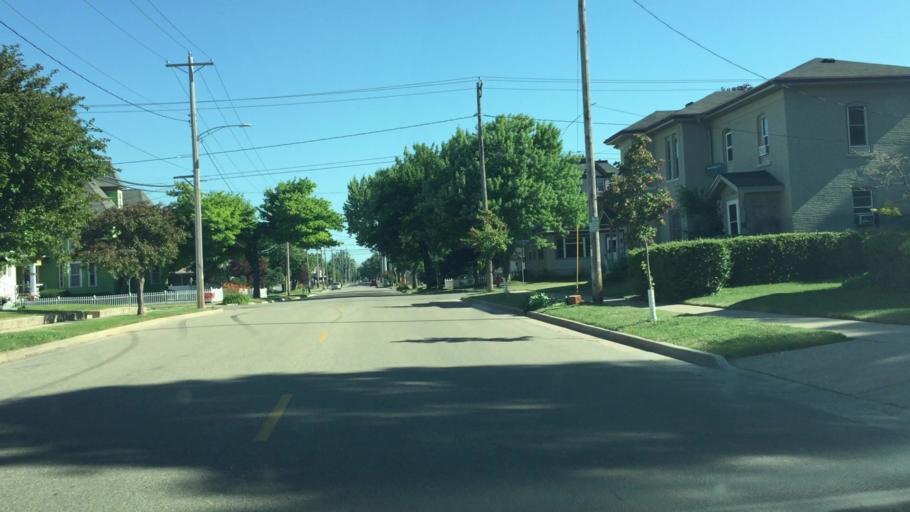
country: US
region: Wisconsin
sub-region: Winnebago County
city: Menasha
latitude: 44.2024
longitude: -88.4492
